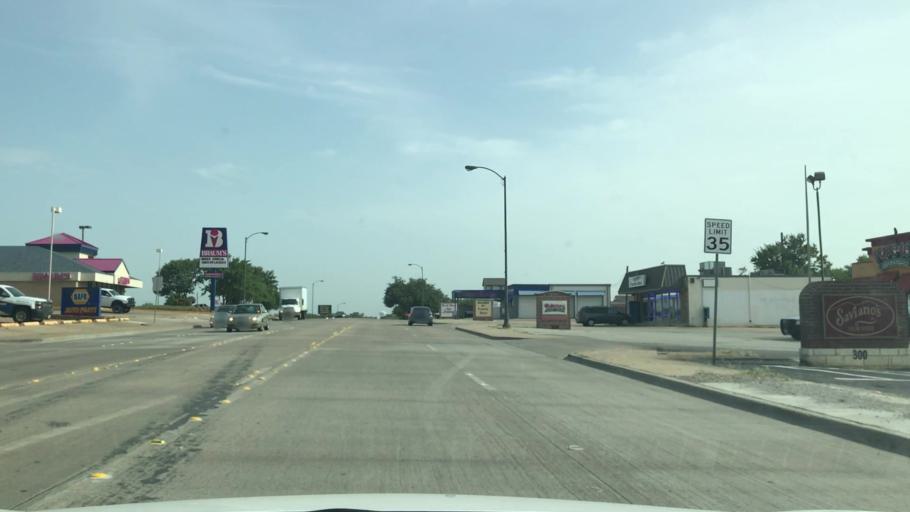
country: US
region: Texas
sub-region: Tarrant County
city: Euless
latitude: 32.8401
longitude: -97.0826
